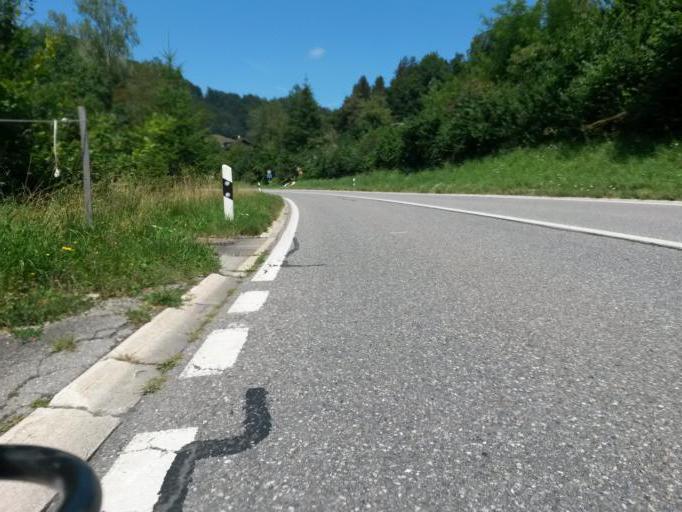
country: CH
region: Bern
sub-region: Bern-Mittelland District
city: Walkringen
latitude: 46.9616
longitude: 7.6235
